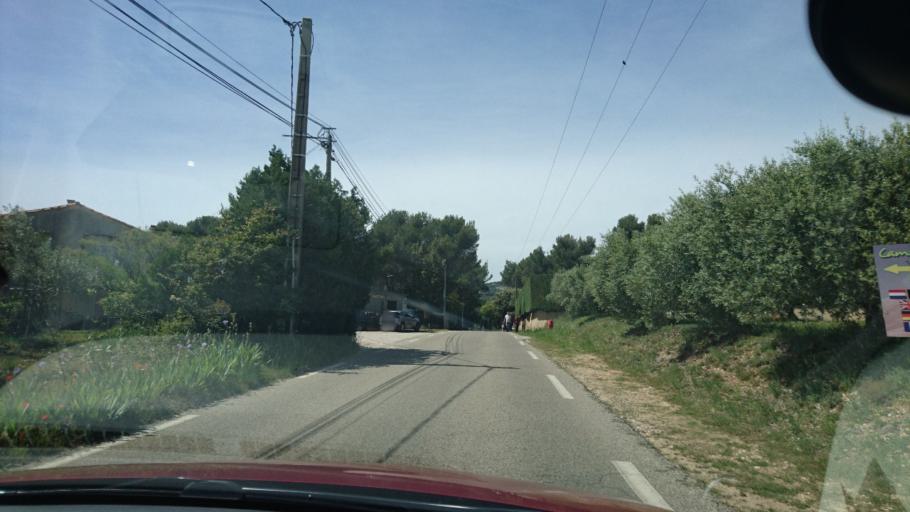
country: FR
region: Provence-Alpes-Cote d'Azur
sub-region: Departement du Vaucluse
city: Bedoin
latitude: 44.1315
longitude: 5.1714
